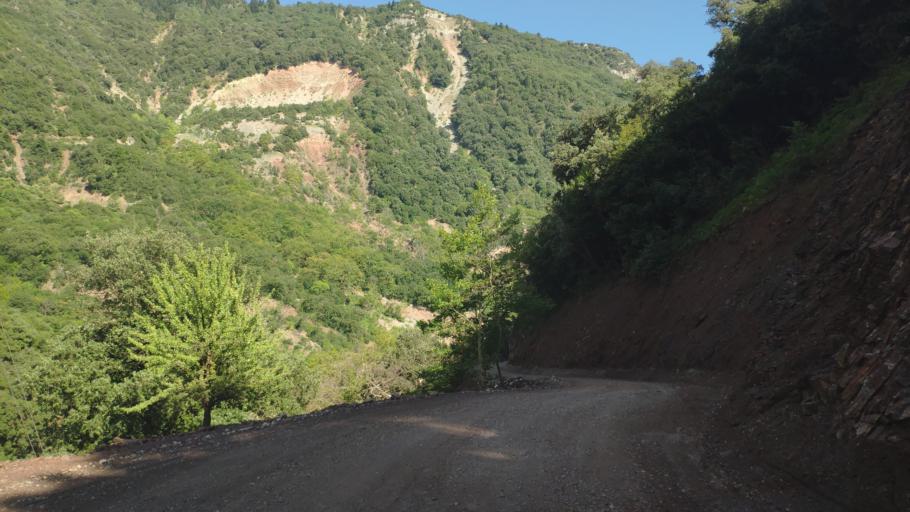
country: GR
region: Central Greece
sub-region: Nomos Evrytanias
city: Kerasochori
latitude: 39.0708
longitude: 21.6043
